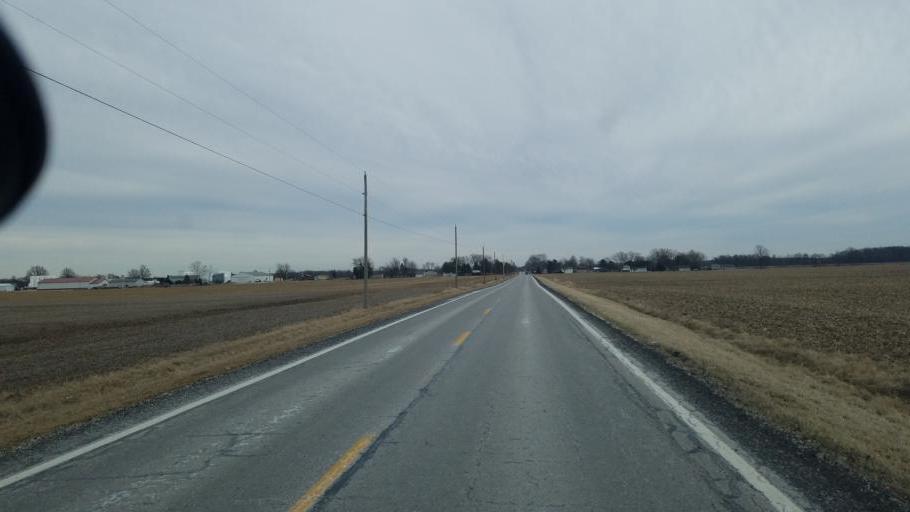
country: US
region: Ohio
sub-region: Marion County
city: Prospect
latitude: 40.4513
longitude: -83.0979
